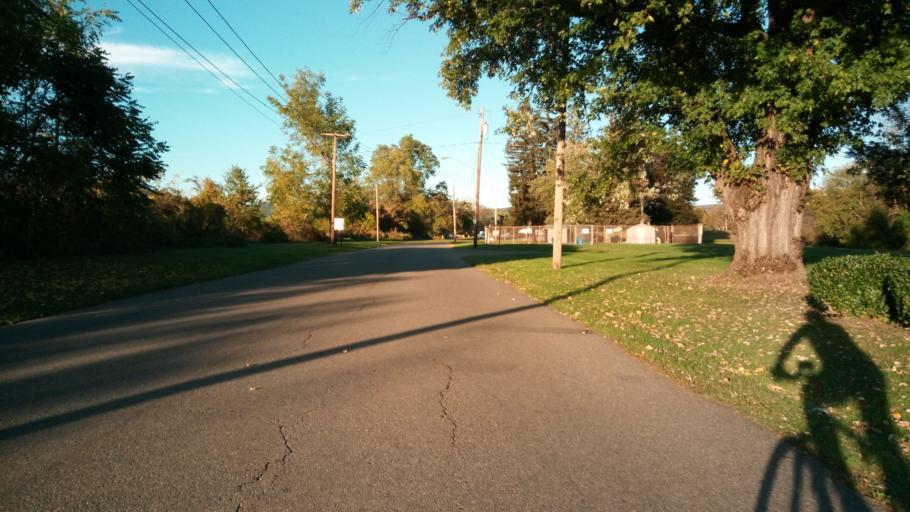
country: US
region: New York
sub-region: Chemung County
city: Elmira
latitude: 42.0787
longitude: -76.8212
